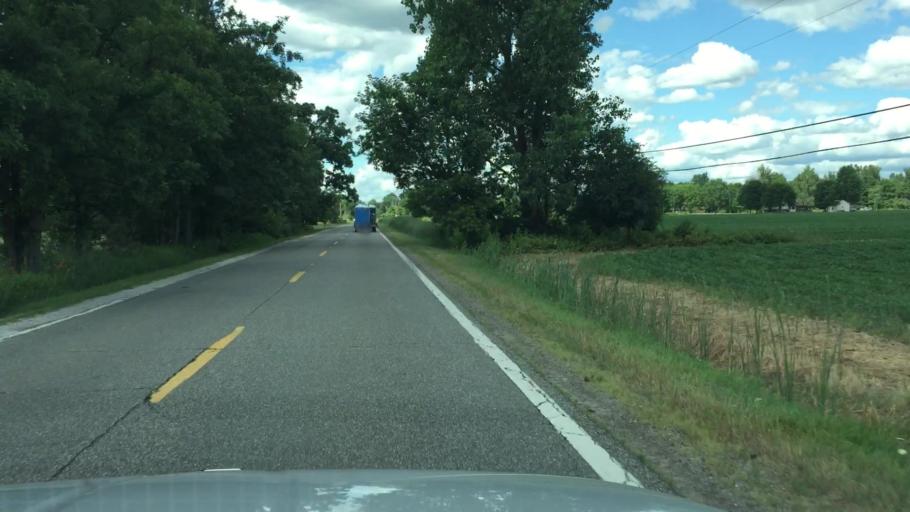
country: US
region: Michigan
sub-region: Macomb County
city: Armada
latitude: 42.8822
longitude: -82.9455
